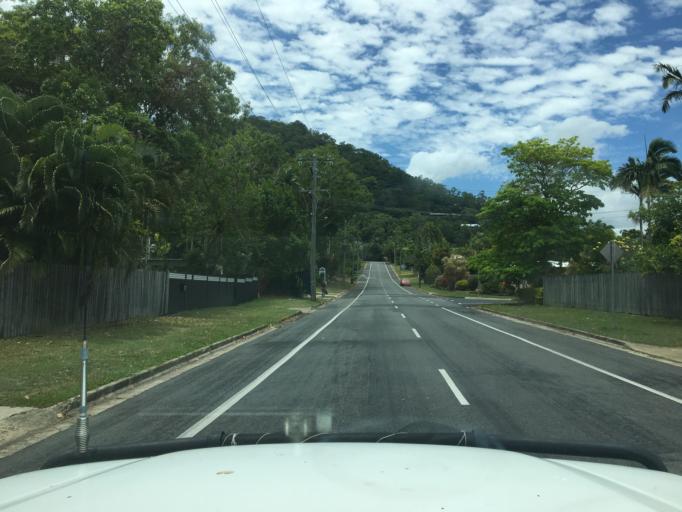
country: AU
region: Queensland
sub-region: Cairns
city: Trinity Beach
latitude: -16.7885
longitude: 145.6961
